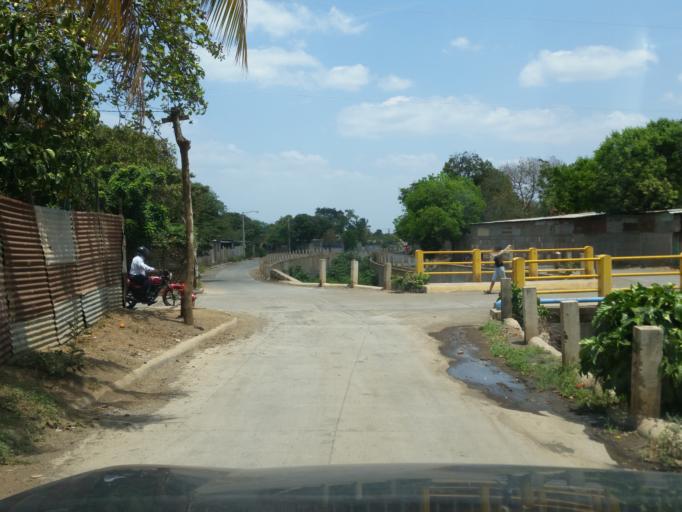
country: NI
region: Managua
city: Managua
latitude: 12.1350
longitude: -86.1895
